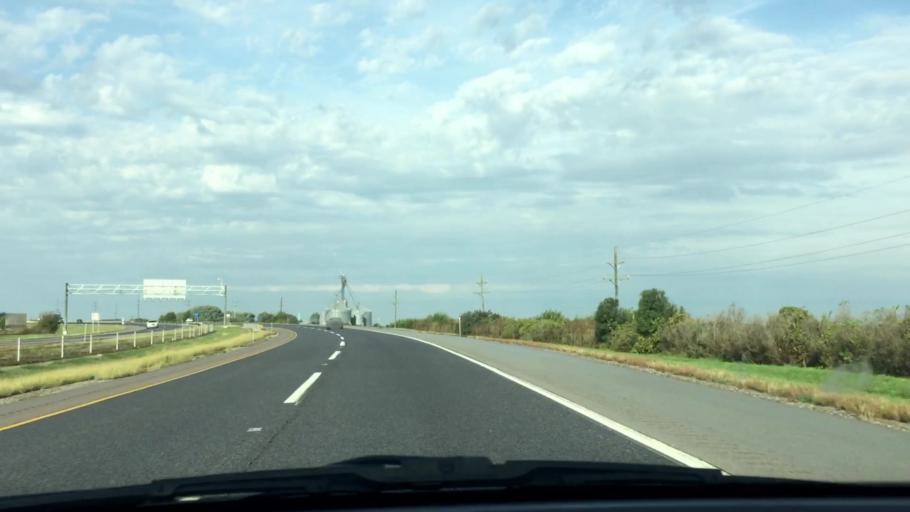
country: US
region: Illinois
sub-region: Lee County
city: Dixon
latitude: 41.8261
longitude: -89.4461
